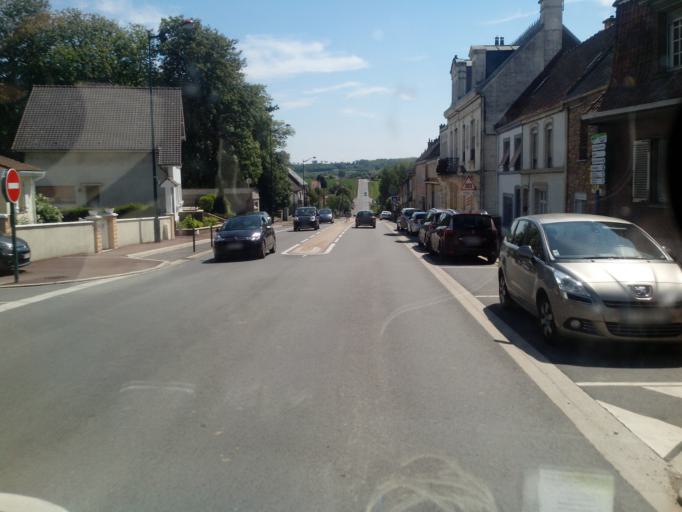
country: FR
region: Nord-Pas-de-Calais
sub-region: Departement du Pas-de-Calais
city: Samer
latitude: 50.6375
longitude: 1.7430
